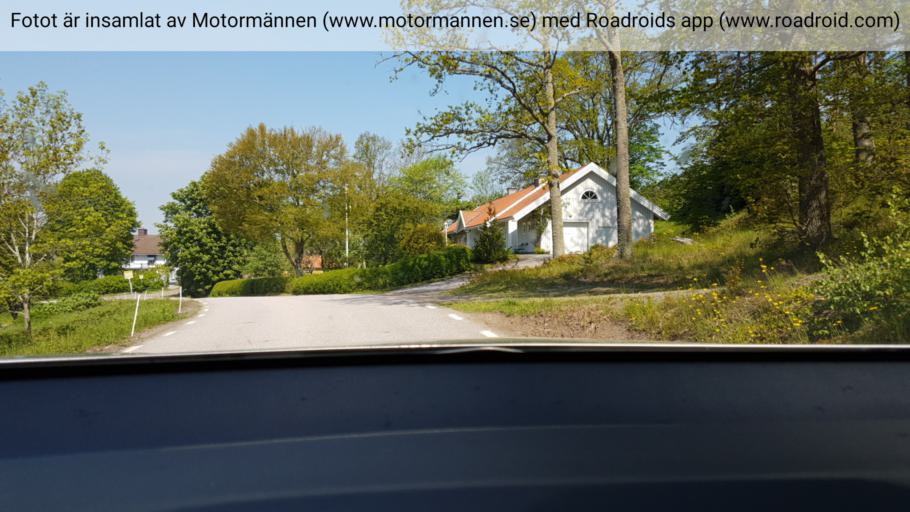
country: SE
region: Kalmar
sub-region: Vasterviks Kommun
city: Forserum
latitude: 57.8484
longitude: 16.5352
